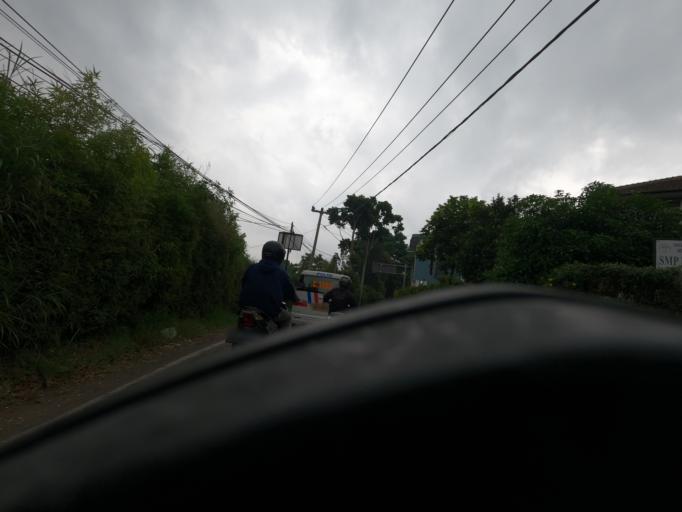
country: ID
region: West Java
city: Lembang
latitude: -6.8164
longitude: 107.6037
